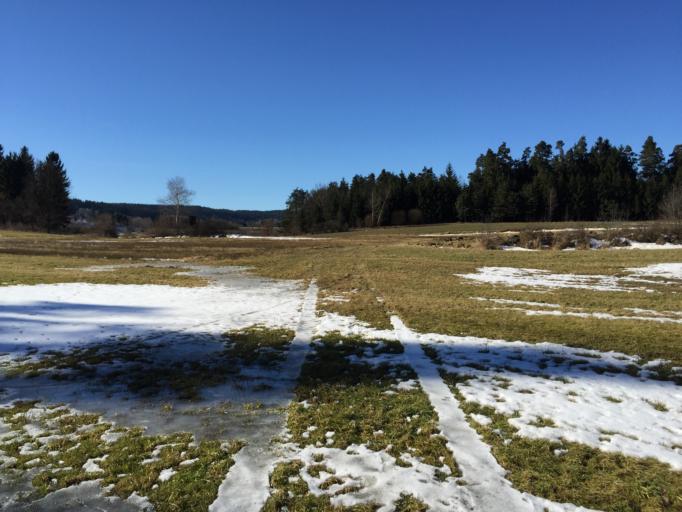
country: AT
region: Lower Austria
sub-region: Politischer Bezirk Gmund
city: Weitra
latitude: 48.6695
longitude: 14.9458
